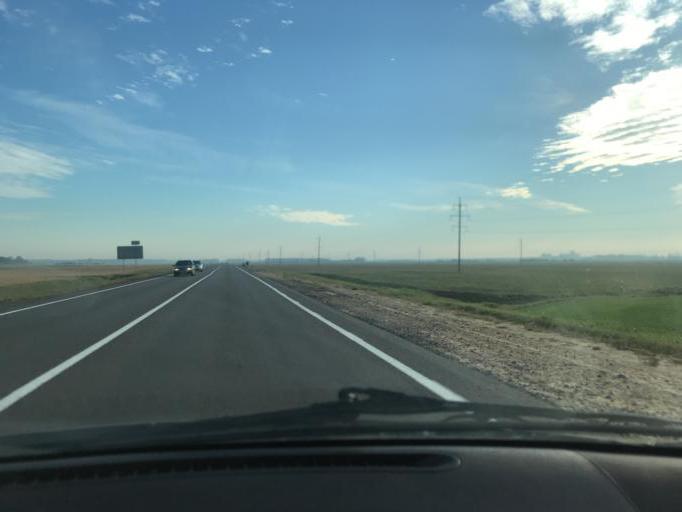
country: BY
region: Brest
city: Drahichyn
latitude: 52.1966
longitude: 25.0262
